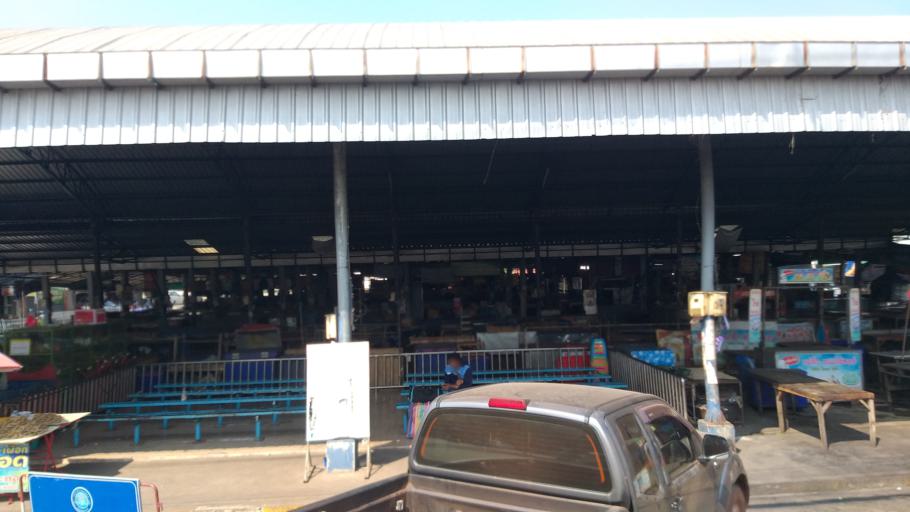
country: TH
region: Changwat Udon Thani
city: Nong Han
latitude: 17.3631
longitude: 103.1068
